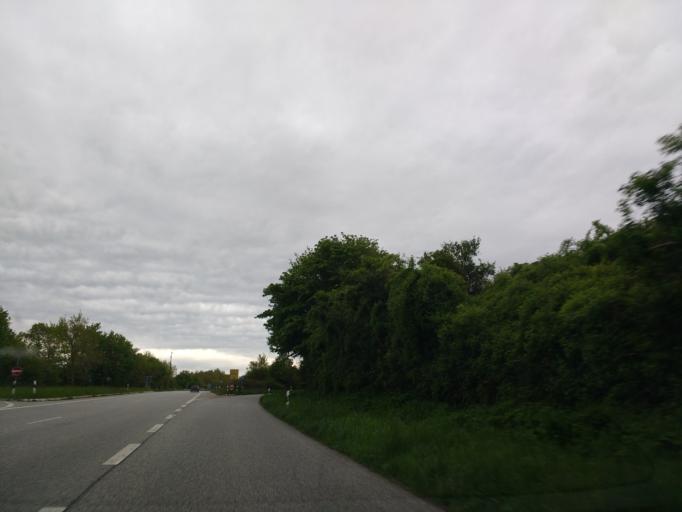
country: DE
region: Schleswig-Holstein
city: Damp
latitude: 54.5768
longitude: 9.9570
